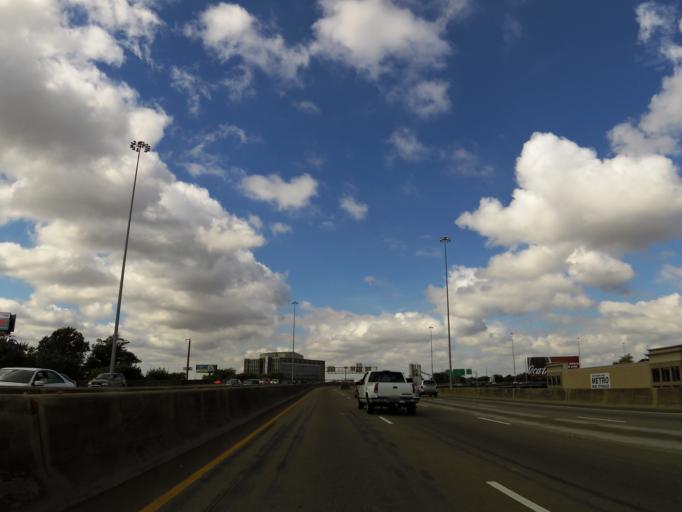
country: US
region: Alabama
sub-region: Jefferson County
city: Birmingham
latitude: 33.5211
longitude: -86.8149
